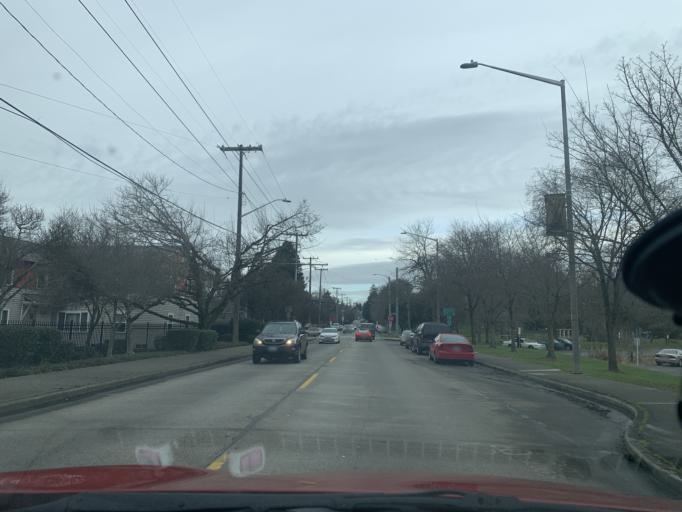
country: US
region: Washington
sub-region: King County
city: Bryn Mawr-Skyway
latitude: 47.5225
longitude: -122.2645
